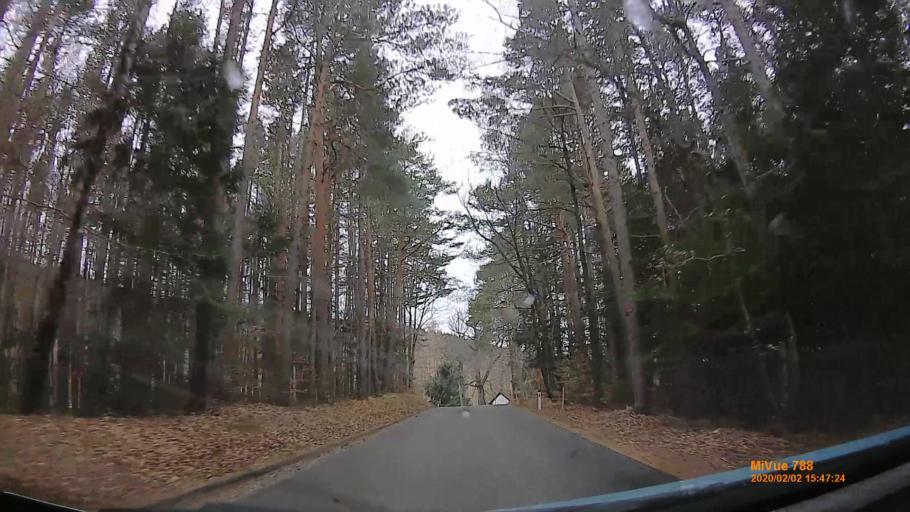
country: AT
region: Lower Austria
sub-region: Politischer Bezirk Neunkirchen
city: Reichenau an der Rax
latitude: 47.6897
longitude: 15.8152
